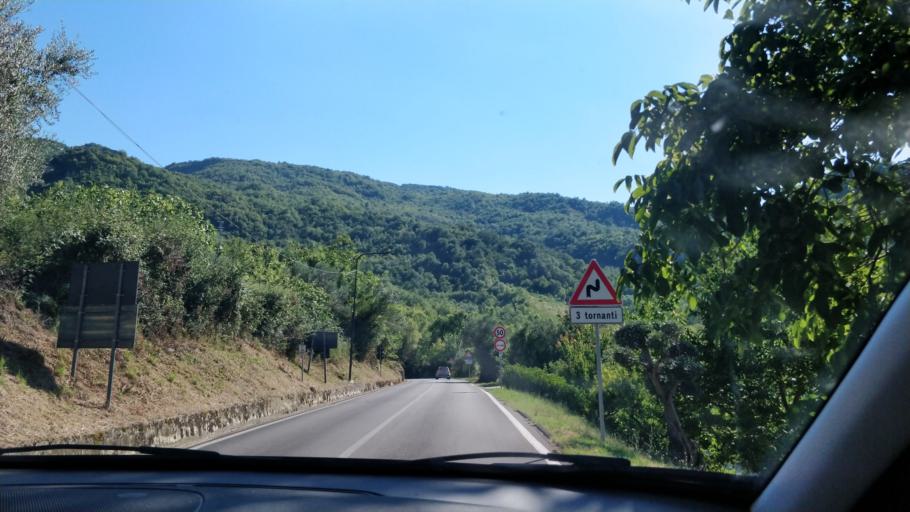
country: IT
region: Abruzzo
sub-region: Provincia di Pescara
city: Serramonacesca
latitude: 42.2480
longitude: 14.0914
